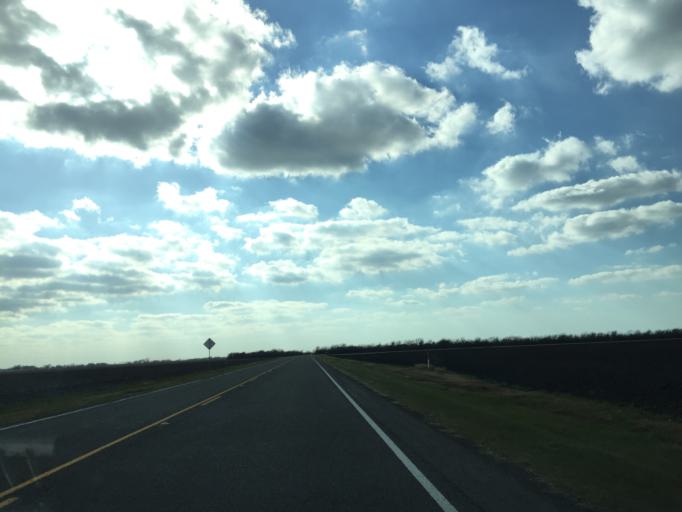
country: US
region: Texas
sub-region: Williamson County
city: Taylor
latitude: 30.6406
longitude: -97.4111
